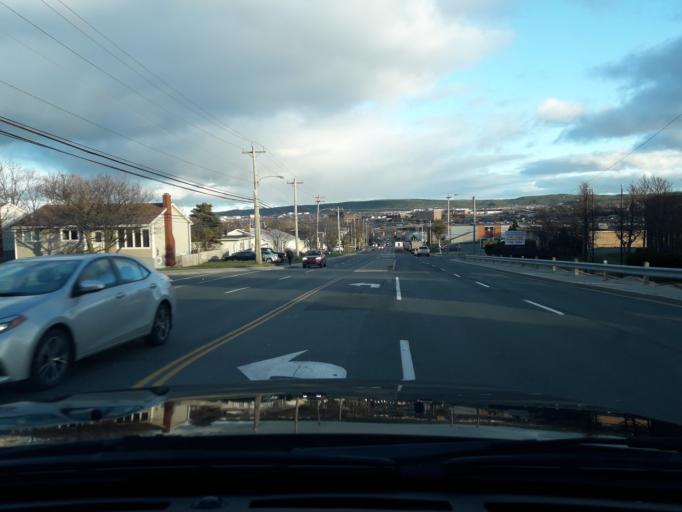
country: CA
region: Newfoundland and Labrador
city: St. John's
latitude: 47.5633
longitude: -52.7585
